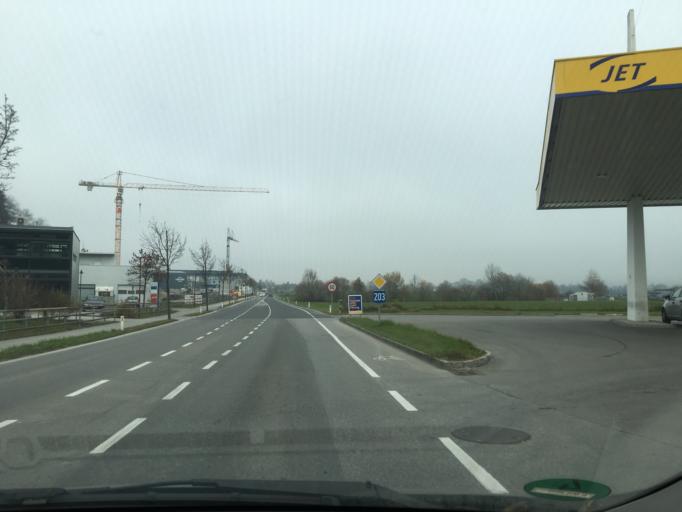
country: AT
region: Vorarlberg
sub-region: Politischer Bezirk Feldkirch
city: Altach
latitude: 47.3447
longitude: 9.6562
